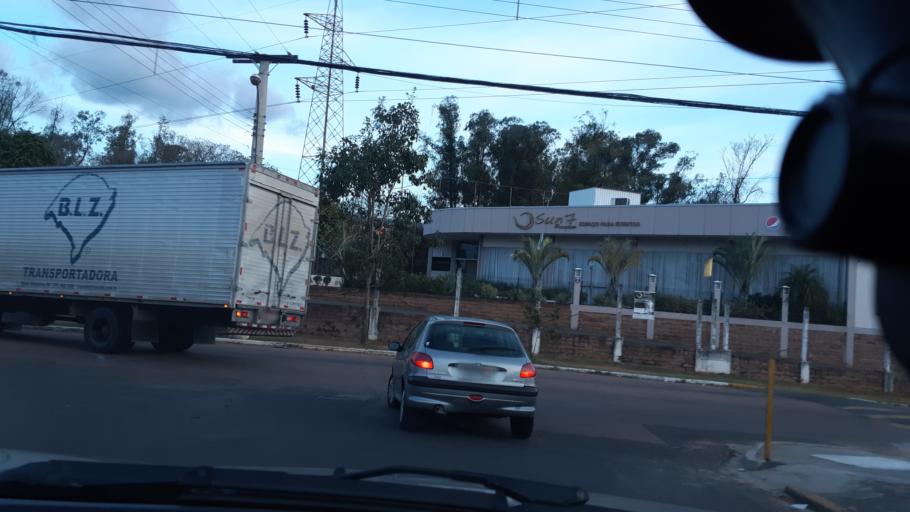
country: BR
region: Rio Grande do Sul
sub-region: Sapucaia Do Sul
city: Sapucaia
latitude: -29.8440
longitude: -51.1498
